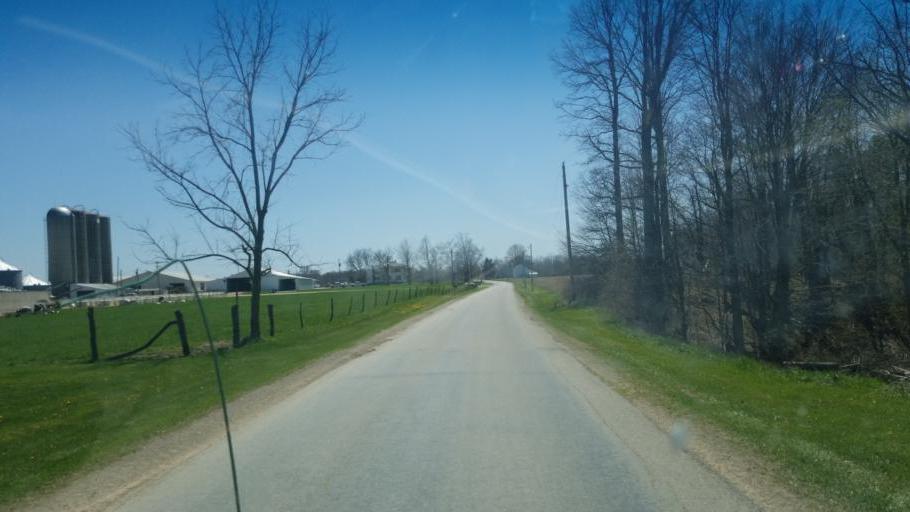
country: US
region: Ohio
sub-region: Huron County
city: Greenwich
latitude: 41.0524
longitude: -82.5114
